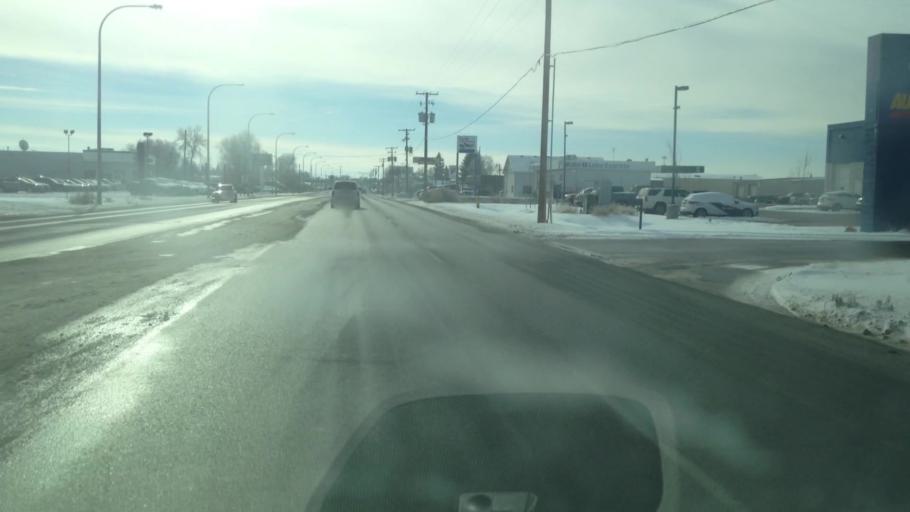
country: US
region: Idaho
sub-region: Bonneville County
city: Idaho Falls
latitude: 43.5183
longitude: -112.0236
